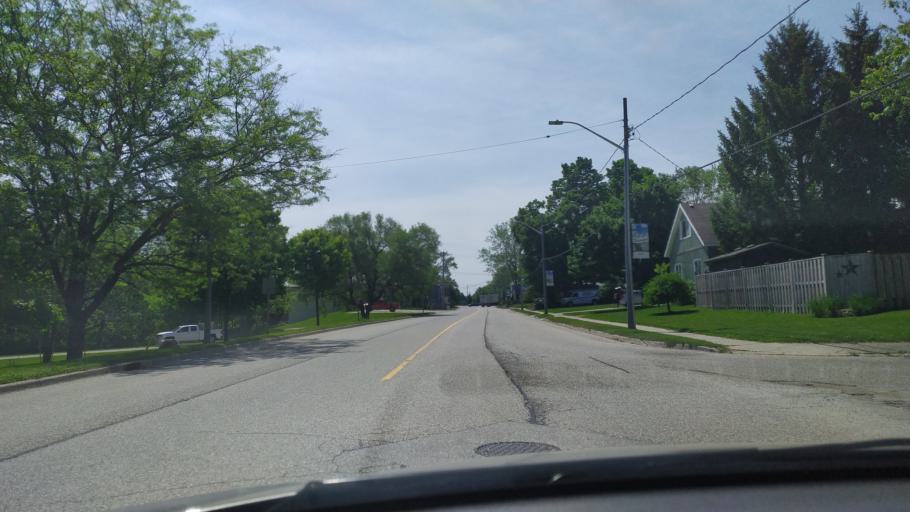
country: CA
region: Ontario
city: Dorchester
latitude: 43.0610
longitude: -80.9974
